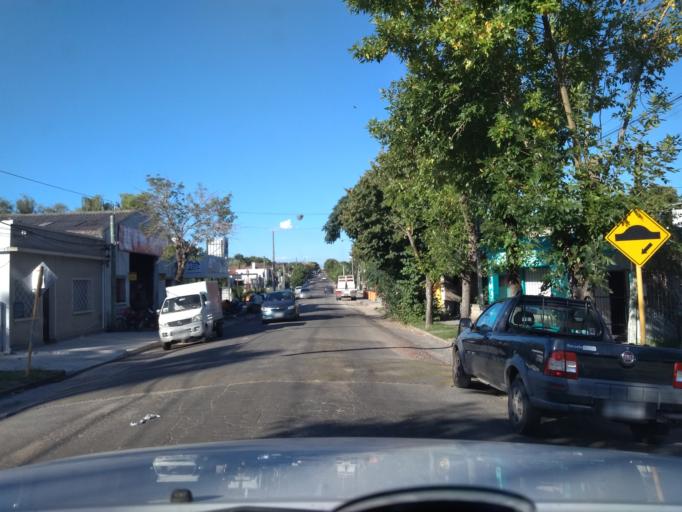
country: UY
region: Florida
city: Florida
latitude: -34.0974
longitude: -56.2251
